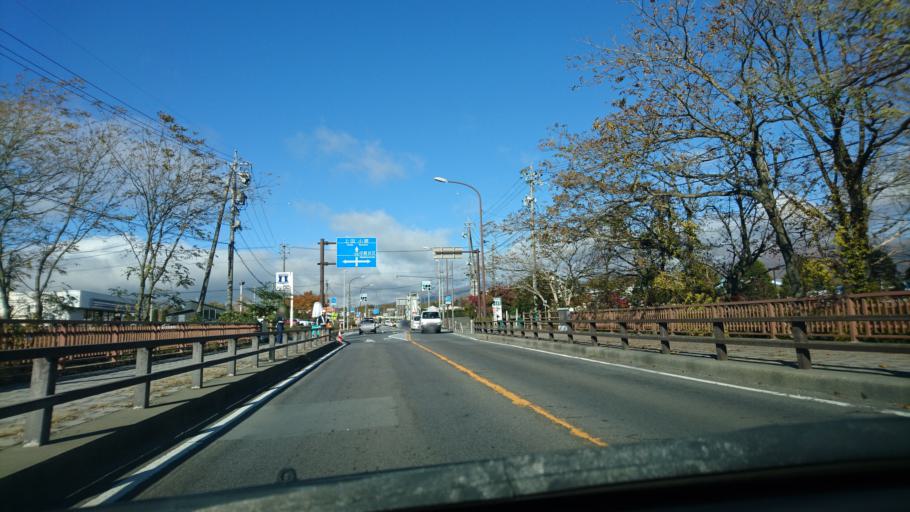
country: JP
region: Nagano
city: Komoro
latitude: 36.3370
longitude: 138.5931
